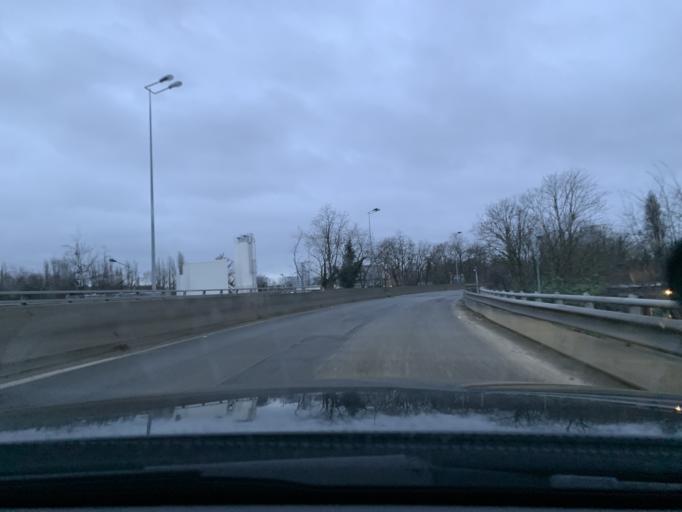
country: FR
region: Ile-de-France
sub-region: Departement de Seine-Saint-Denis
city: Saint-Denis
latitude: 48.9337
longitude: 2.3721
